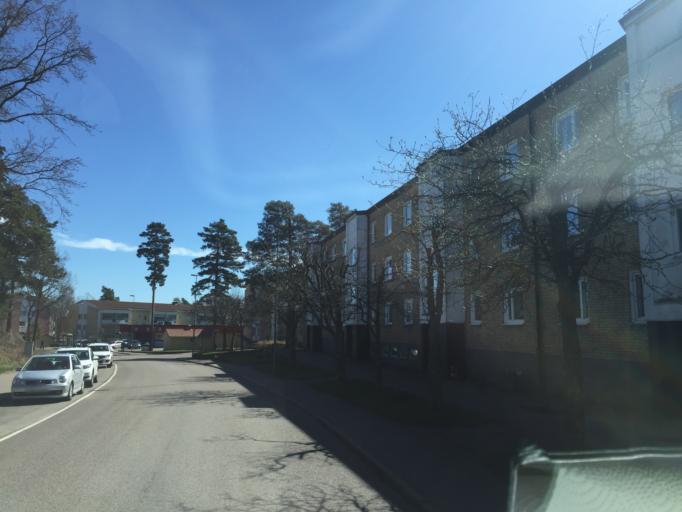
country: SE
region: Kalmar
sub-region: Oskarshamns Kommun
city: Oskarshamn
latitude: 57.2558
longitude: 16.4445
